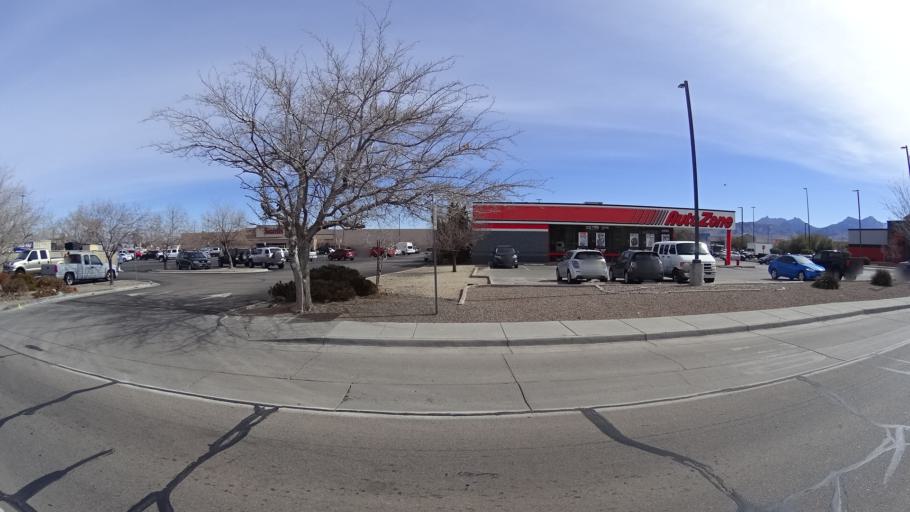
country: US
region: Arizona
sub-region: Mohave County
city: Kingman
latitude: 35.2234
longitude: -114.0360
